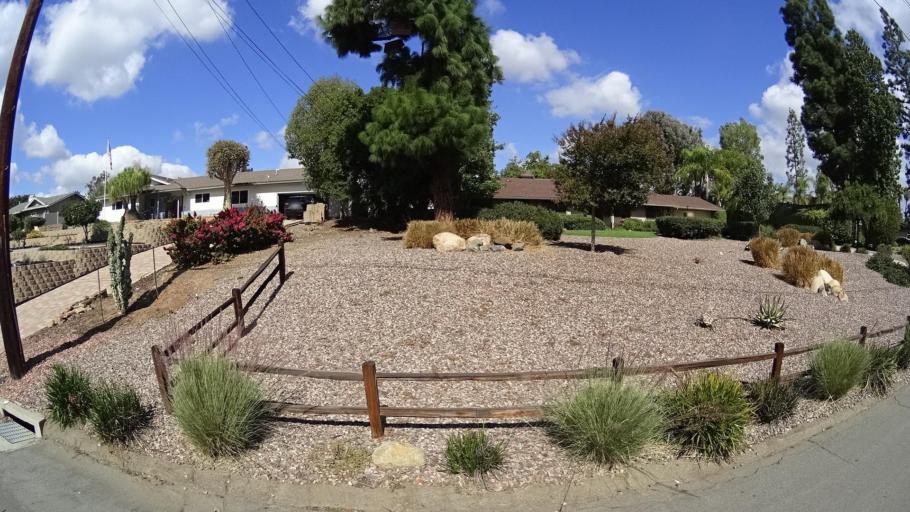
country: US
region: California
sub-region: San Diego County
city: Rancho San Diego
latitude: 32.7601
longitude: -116.9473
